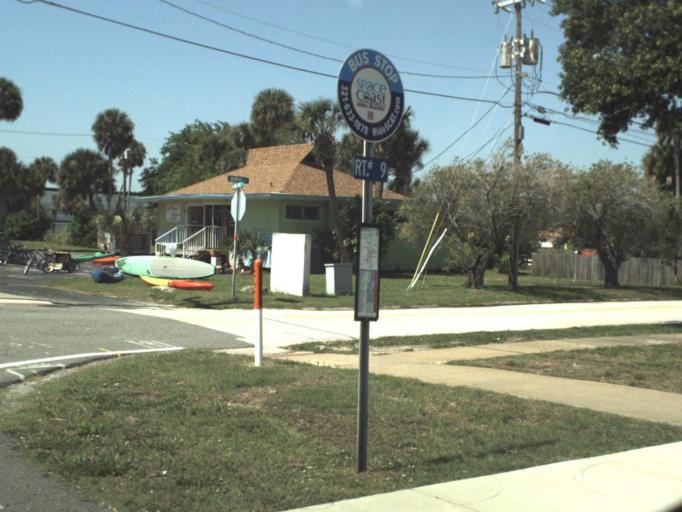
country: US
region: Florida
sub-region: Brevard County
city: Cocoa Beach
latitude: 28.3407
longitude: -80.6101
